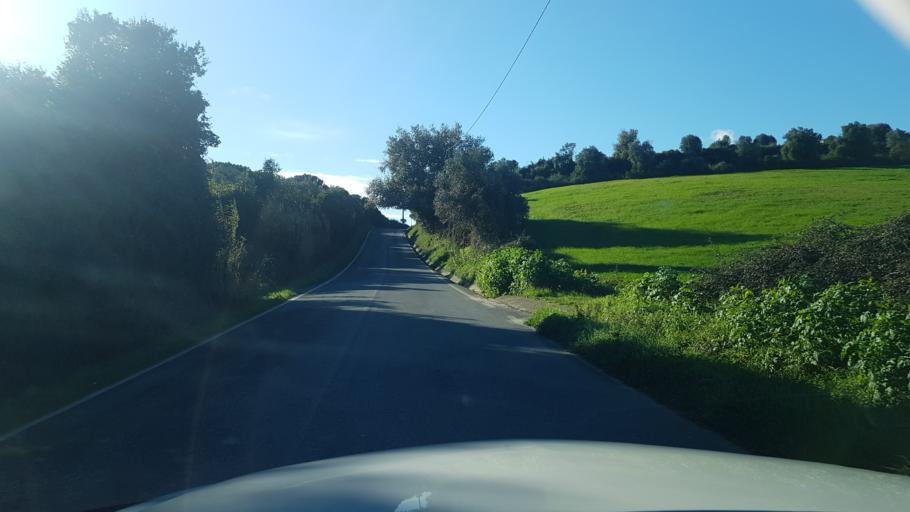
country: PT
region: Santarem
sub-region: Torres Novas
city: Torres Novas
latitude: 39.4750
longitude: -8.5226
